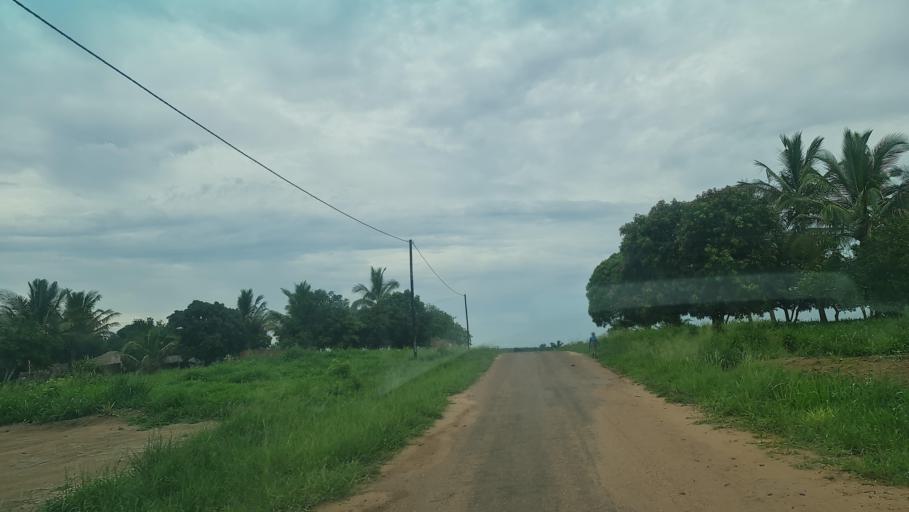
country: MW
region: Southern Region
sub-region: Nsanje District
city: Nsanje
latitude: -17.6770
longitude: 35.7215
